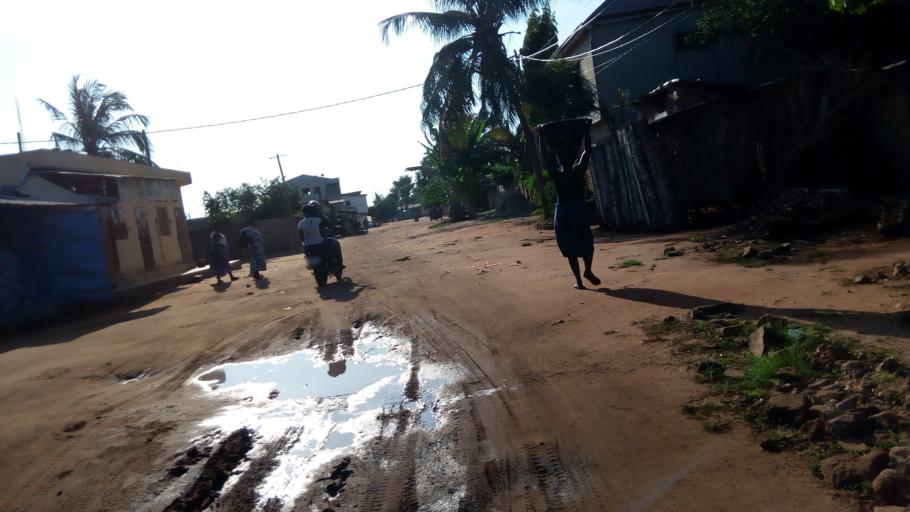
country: TG
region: Maritime
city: Lome
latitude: 6.2304
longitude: 1.1911
